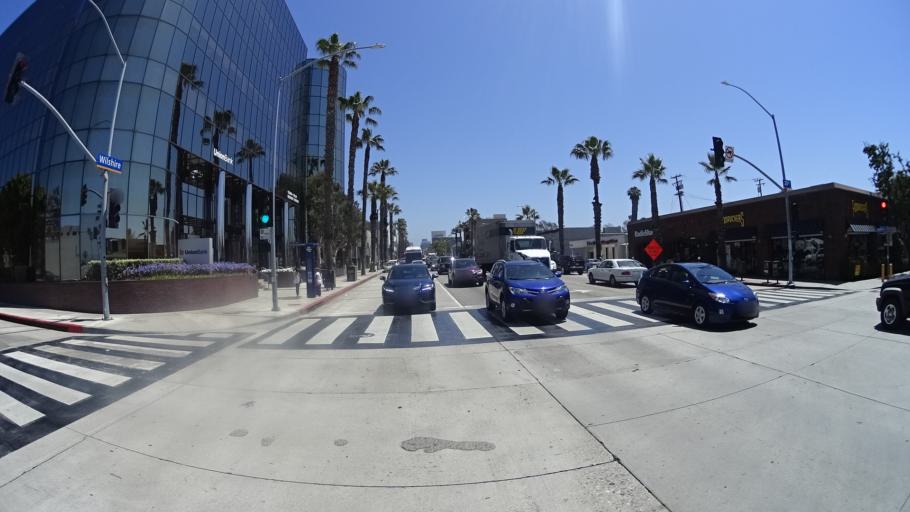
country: US
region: California
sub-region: Los Angeles County
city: Santa Monica
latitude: 34.0315
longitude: -118.4832
